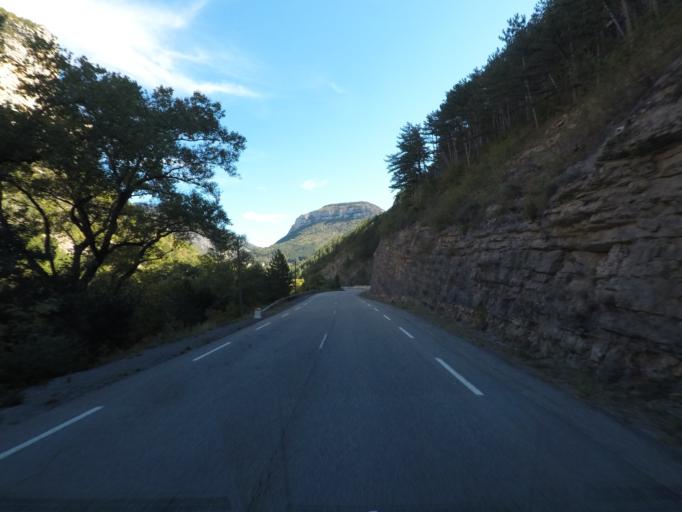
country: FR
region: Rhone-Alpes
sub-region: Departement de la Drome
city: Buis-les-Baronnies
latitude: 44.4138
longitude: 5.3398
